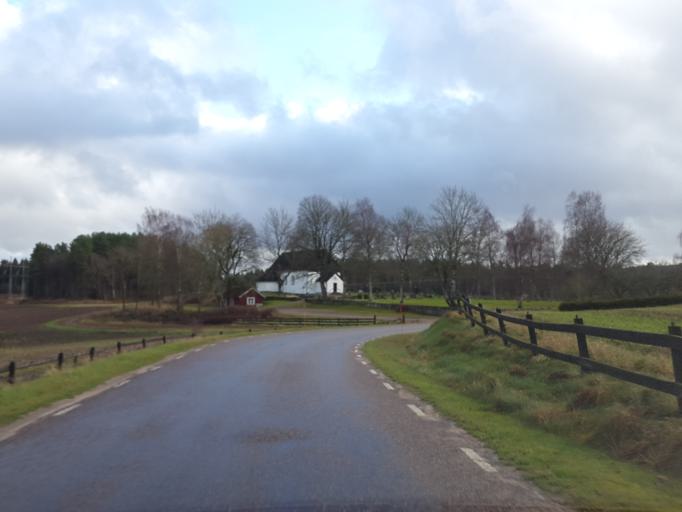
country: SE
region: Vaestra Goetaland
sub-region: Vargarda Kommun
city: Jonstorp
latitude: 57.9948
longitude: 12.7685
